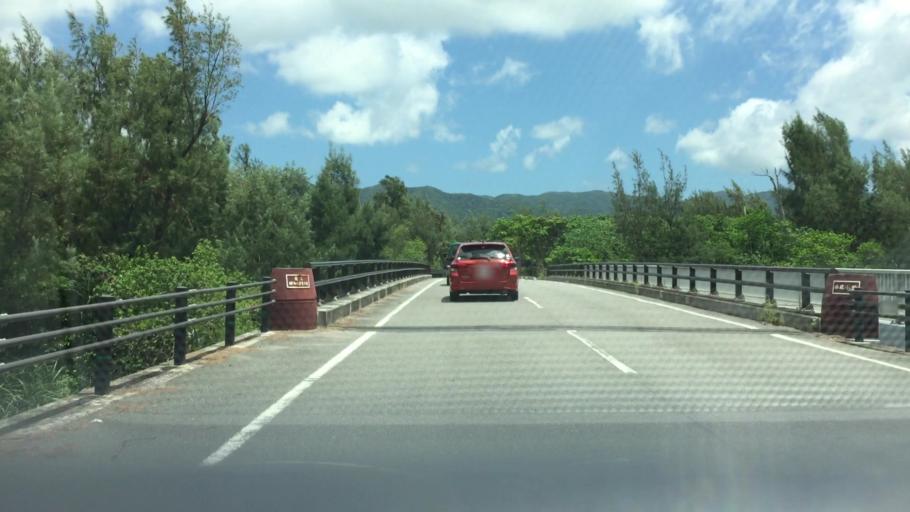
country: JP
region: Okinawa
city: Ishigaki
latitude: 24.3917
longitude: 124.1414
